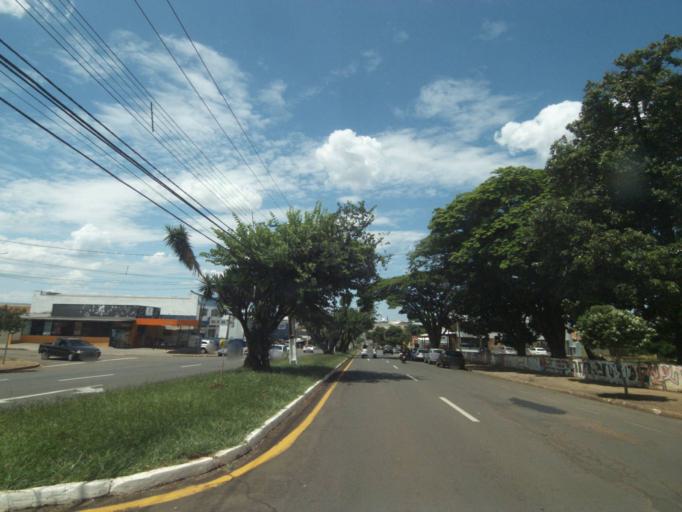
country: BR
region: Parana
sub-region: Londrina
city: Londrina
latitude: -23.3045
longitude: -51.1980
